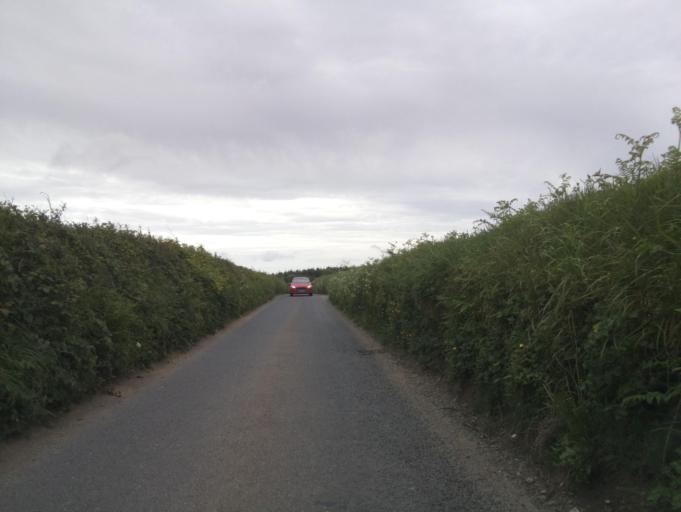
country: GB
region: England
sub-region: Devon
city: Dartmouth
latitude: 50.3367
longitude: -3.6505
